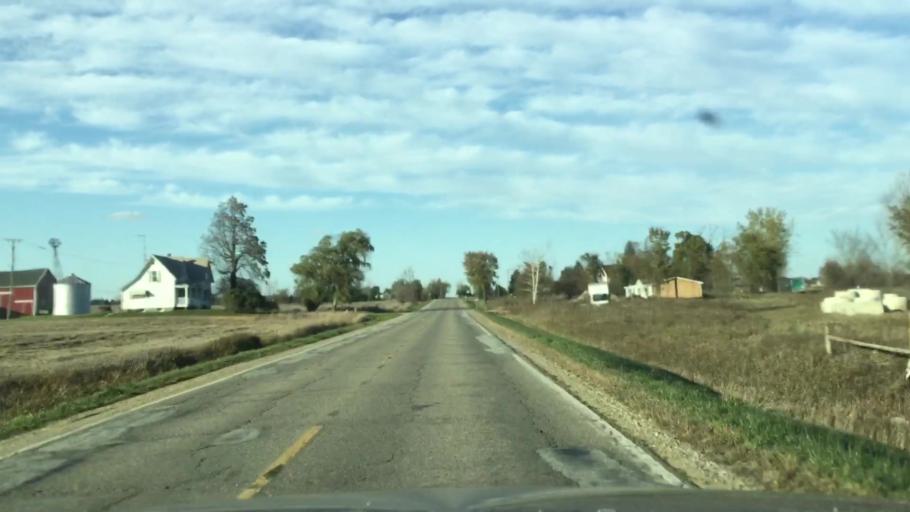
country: US
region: Michigan
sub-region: Lapeer County
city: North Branch
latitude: 43.2545
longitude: -83.1977
